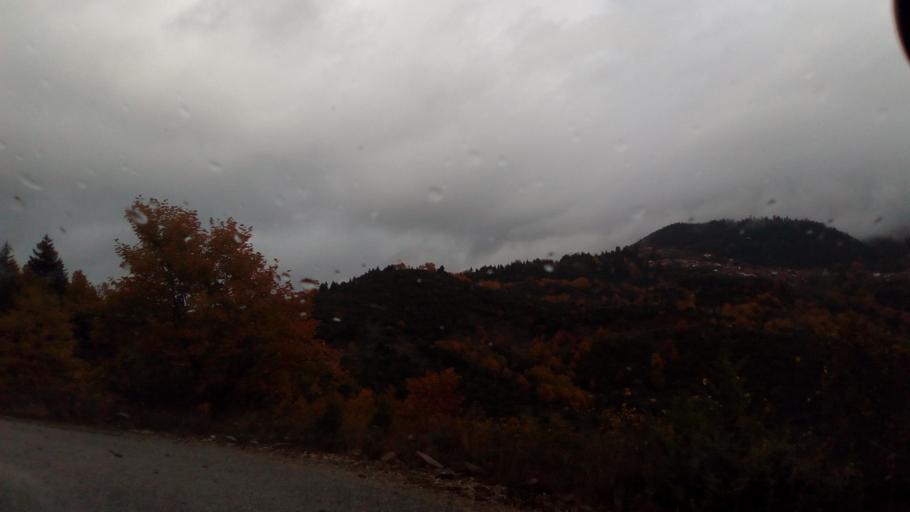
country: GR
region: West Greece
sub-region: Nomos Aitolias kai Akarnanias
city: Thermo
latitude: 38.6780
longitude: 21.8546
